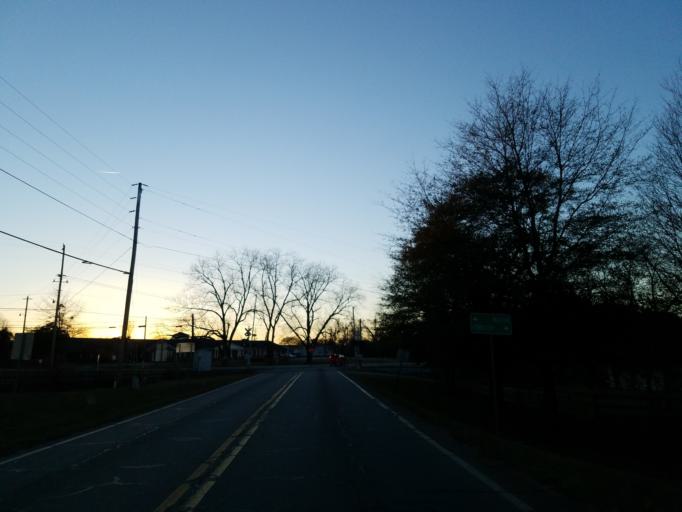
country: US
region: Georgia
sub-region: Monroe County
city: Forsyth
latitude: 33.0266
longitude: -83.9212
